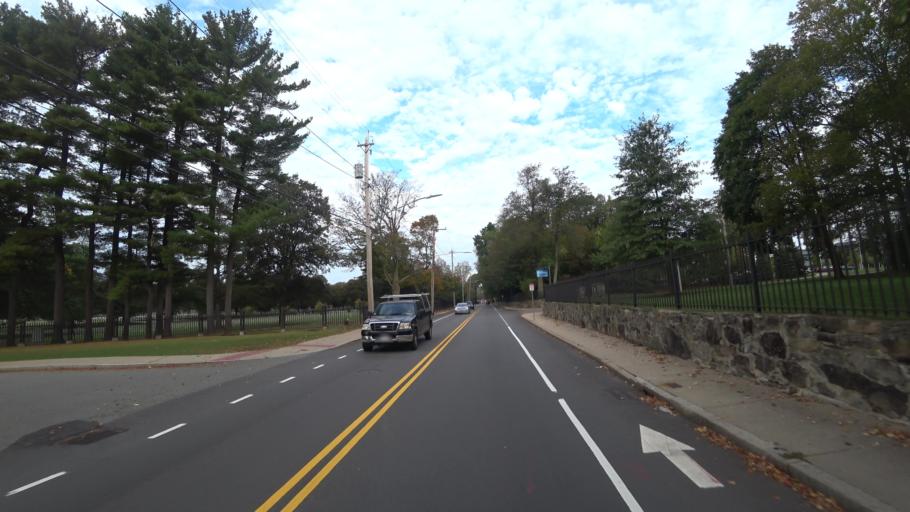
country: US
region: Massachusetts
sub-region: Suffolk County
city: Jamaica Plain
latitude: 42.2843
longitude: -71.1024
